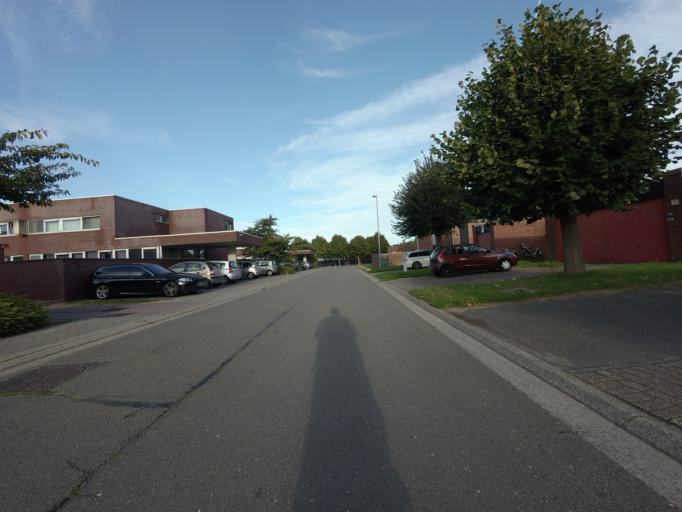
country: BE
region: Flanders
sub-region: Provincie Vlaams-Brabant
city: Herent
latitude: 50.9036
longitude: 4.6821
